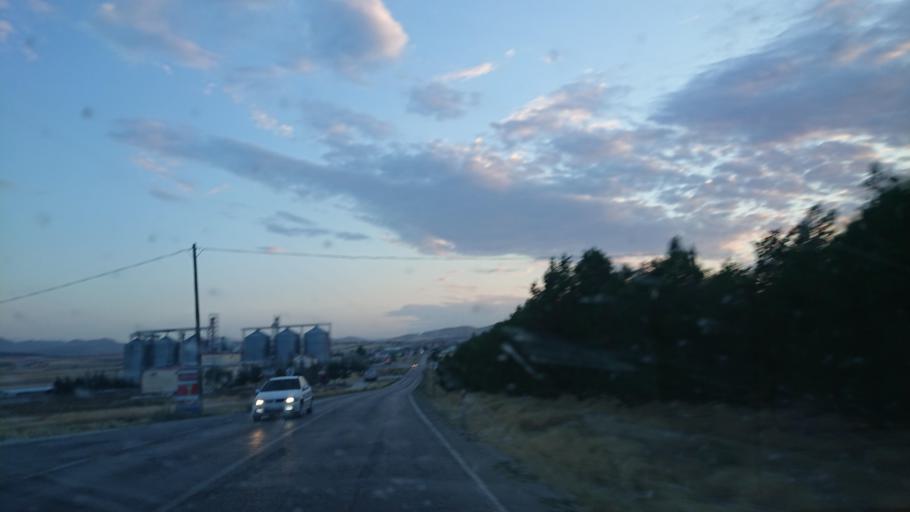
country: TR
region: Aksaray
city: Balci
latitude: 38.7636
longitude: 34.0900
